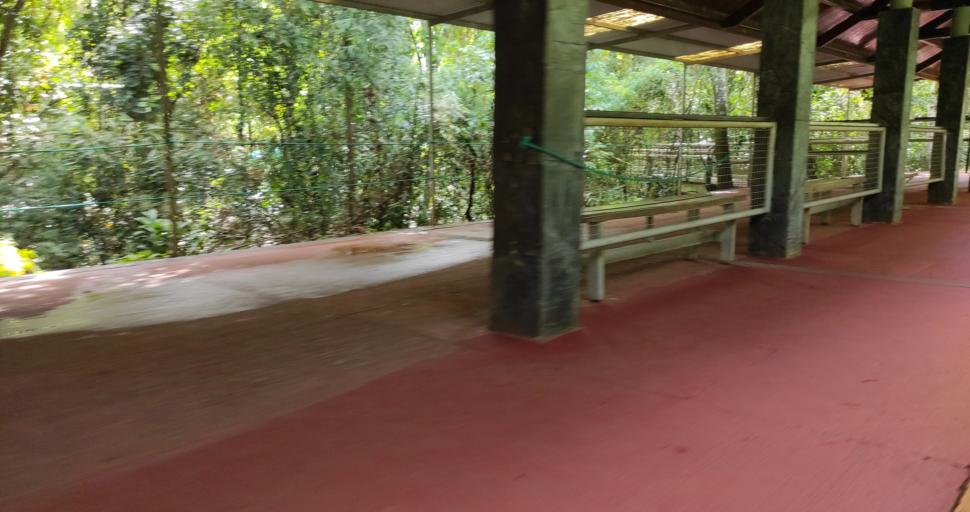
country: AR
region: Misiones
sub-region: Departamento de Iguazu
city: Puerto Iguazu
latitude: -25.7013
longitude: -54.4451
